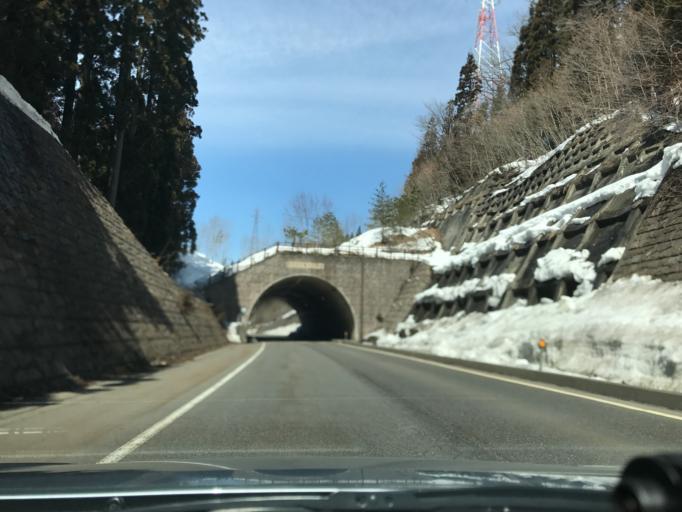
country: JP
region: Nagano
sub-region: Kitaazumi Gun
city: Hakuba
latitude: 36.6156
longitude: 137.8618
